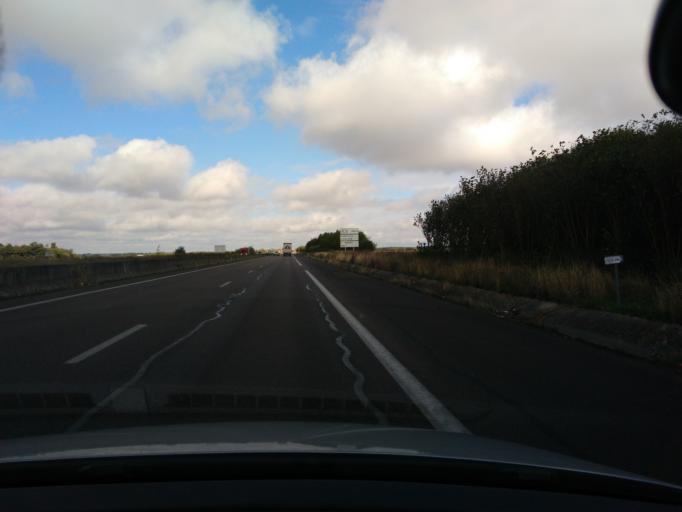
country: FR
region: Haute-Normandie
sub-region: Departement de l'Eure
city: Damville
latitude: 48.8754
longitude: 1.1753
